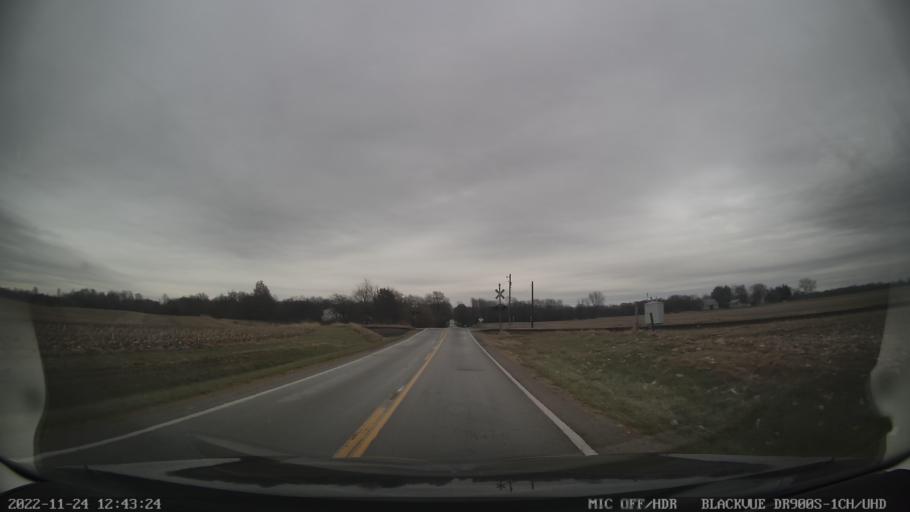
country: US
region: Illinois
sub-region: Macoupin County
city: Staunton
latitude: 38.9615
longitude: -89.7776
